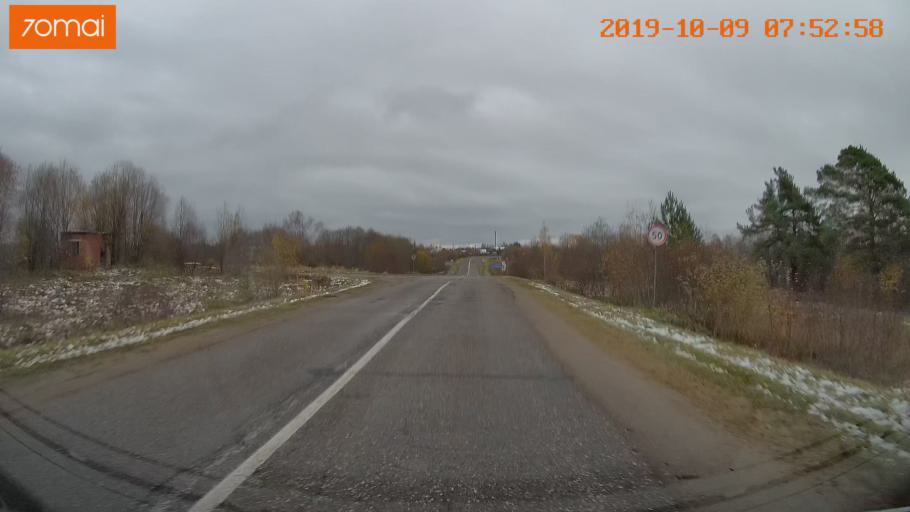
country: RU
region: Jaroslavl
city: Kukoboy
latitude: 58.6952
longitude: 39.8911
